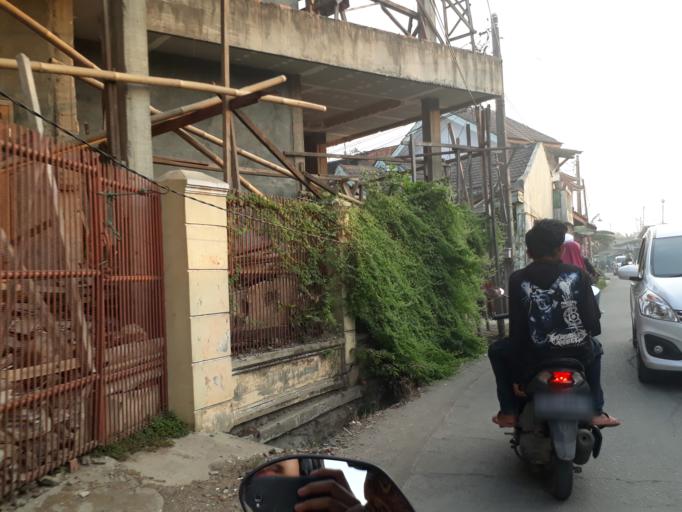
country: ID
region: West Java
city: Bekasi
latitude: -6.2449
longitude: 107.0542
